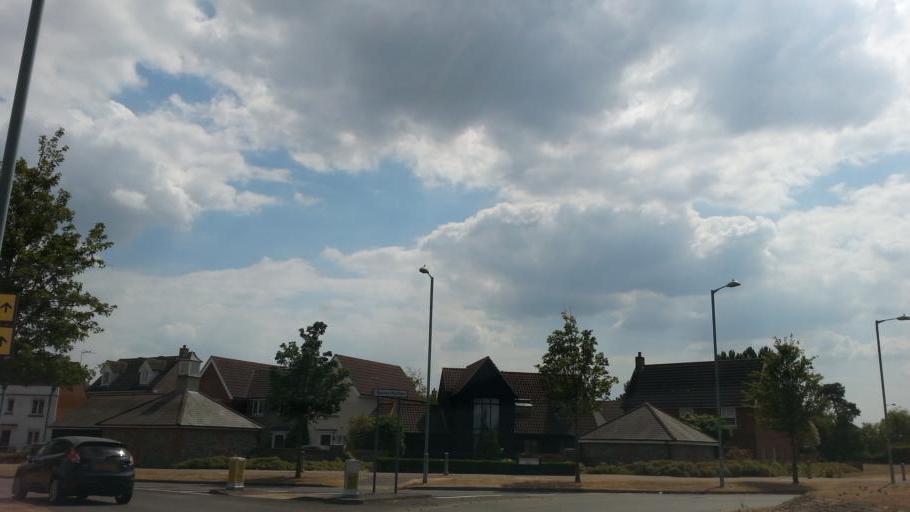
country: GB
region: England
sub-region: Cambridgeshire
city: Isleham
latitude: 52.3093
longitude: 0.4960
